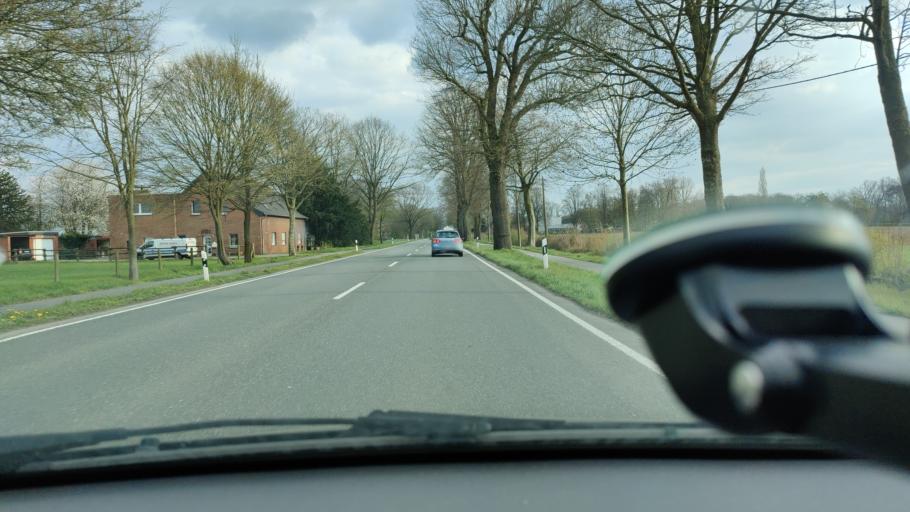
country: DE
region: North Rhine-Westphalia
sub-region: Regierungsbezirk Dusseldorf
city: Wesel
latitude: 51.6990
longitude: 6.6040
